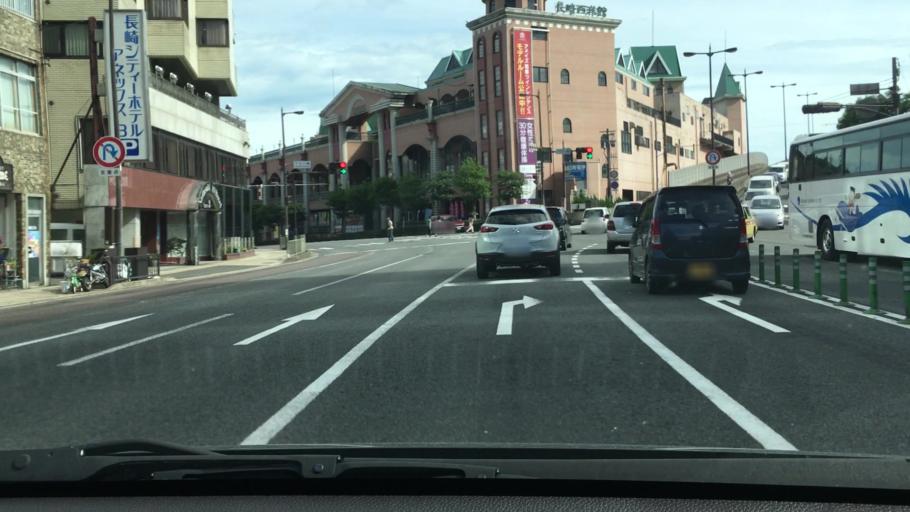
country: JP
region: Nagasaki
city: Nagasaki-shi
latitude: 32.7721
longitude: 129.8629
